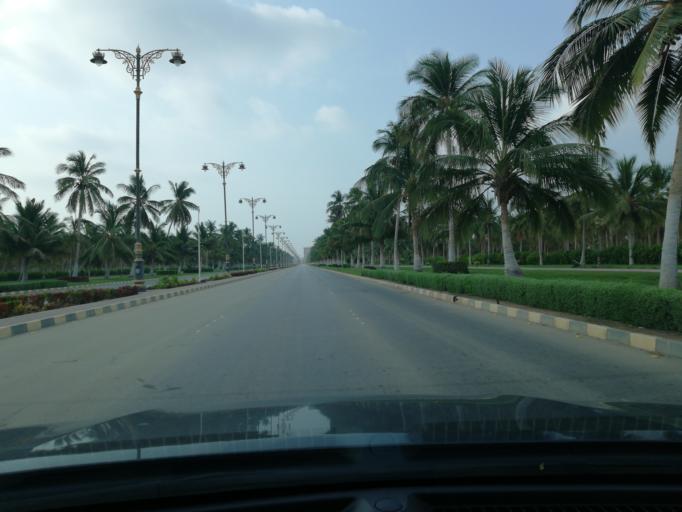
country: OM
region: Zufar
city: Salalah
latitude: 17.0354
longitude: 54.1077
